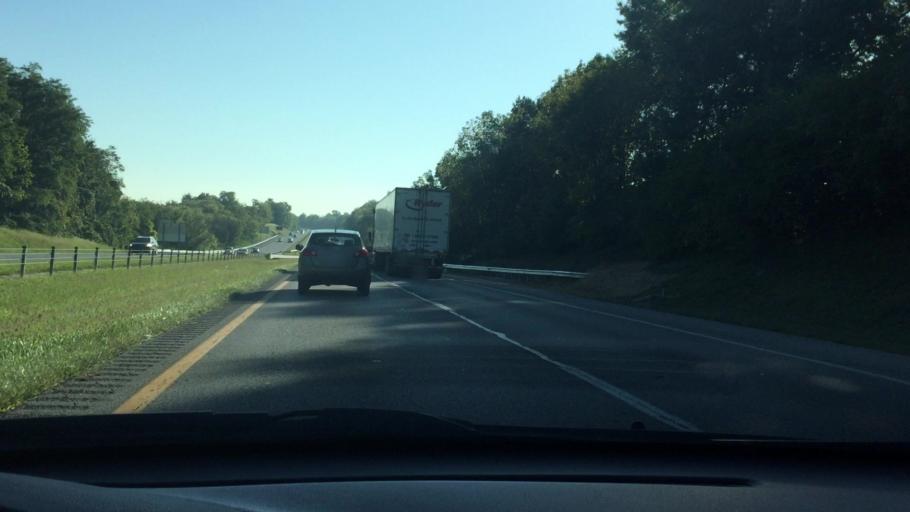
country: US
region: Kentucky
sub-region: Fayette County
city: Lexington
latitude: 37.9918
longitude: -84.4841
